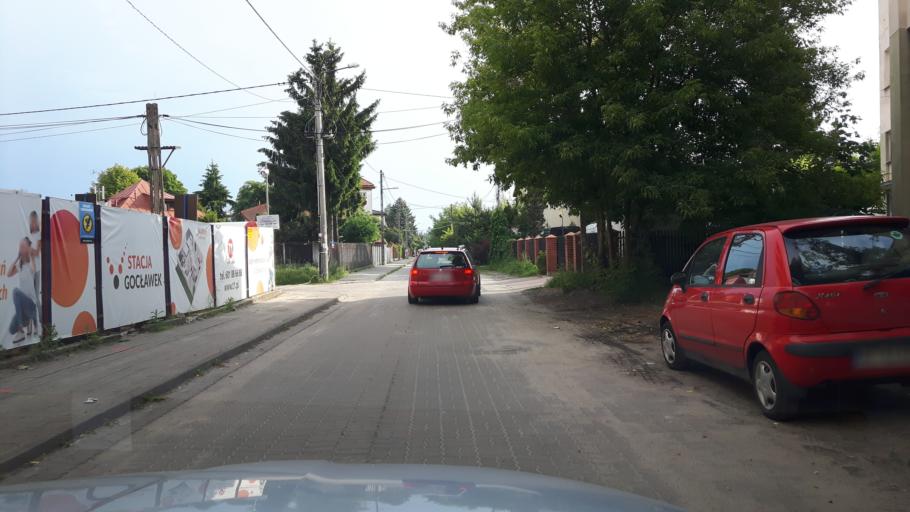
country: PL
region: Masovian Voivodeship
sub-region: Warszawa
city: Rembertow
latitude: 52.2355
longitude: 21.1363
